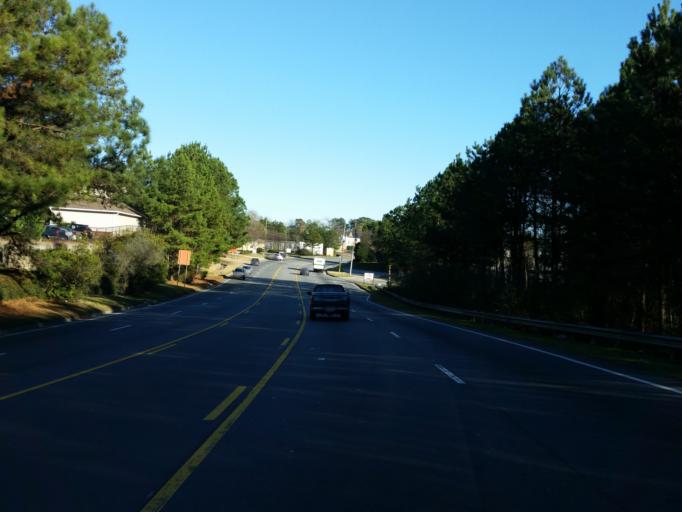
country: US
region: Georgia
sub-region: Cobb County
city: Vinings
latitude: 33.8373
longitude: -84.4783
